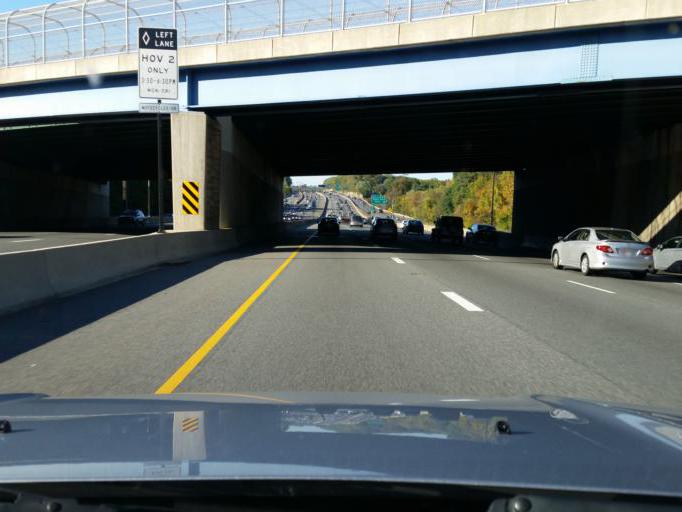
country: US
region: Maryland
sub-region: Montgomery County
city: Rockville
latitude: 39.0855
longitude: -77.1732
